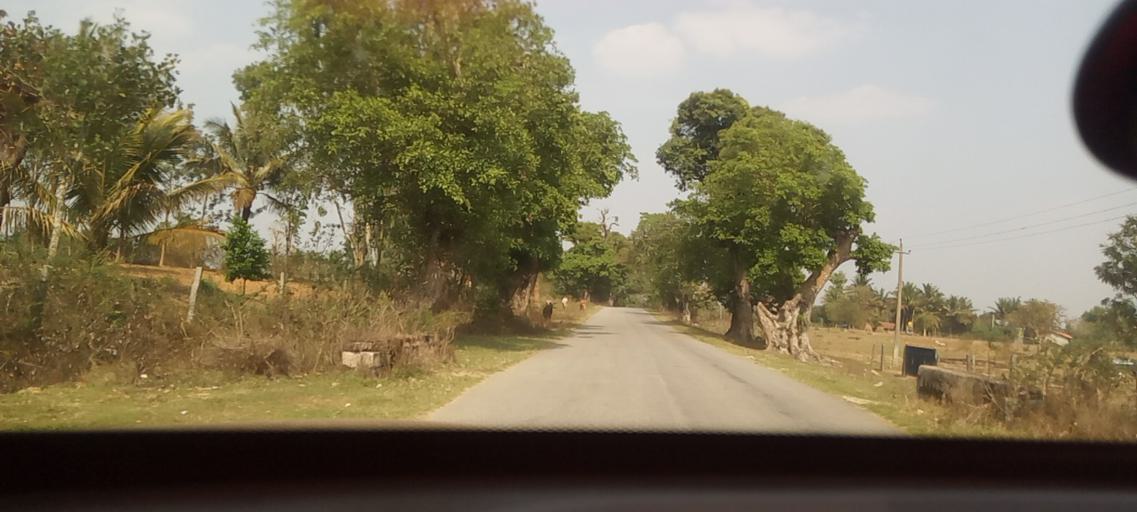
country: IN
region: Karnataka
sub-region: Hassan
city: Belur
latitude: 13.1800
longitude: 75.8272
